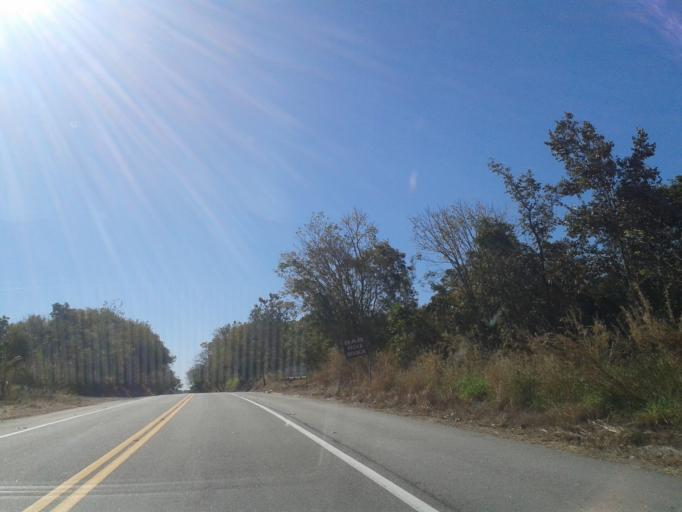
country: BR
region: Goias
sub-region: Goias
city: Goias
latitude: -15.7174
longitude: -50.1888
